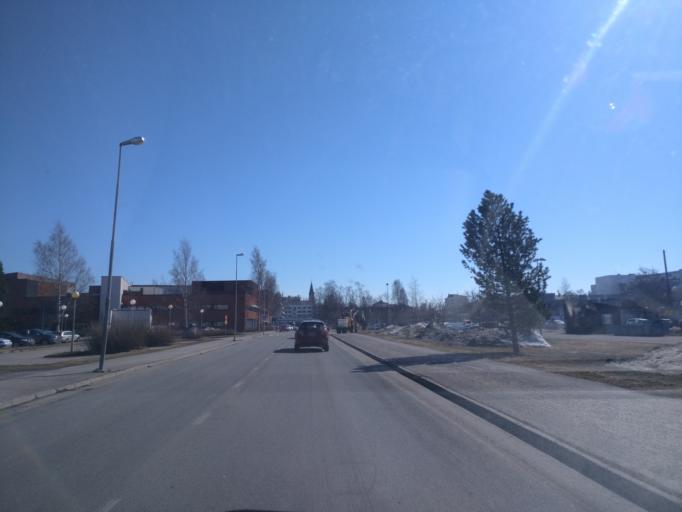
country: FI
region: Lapland
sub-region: Kemi-Tornio
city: Kemi
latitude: 65.7365
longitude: 24.5544
